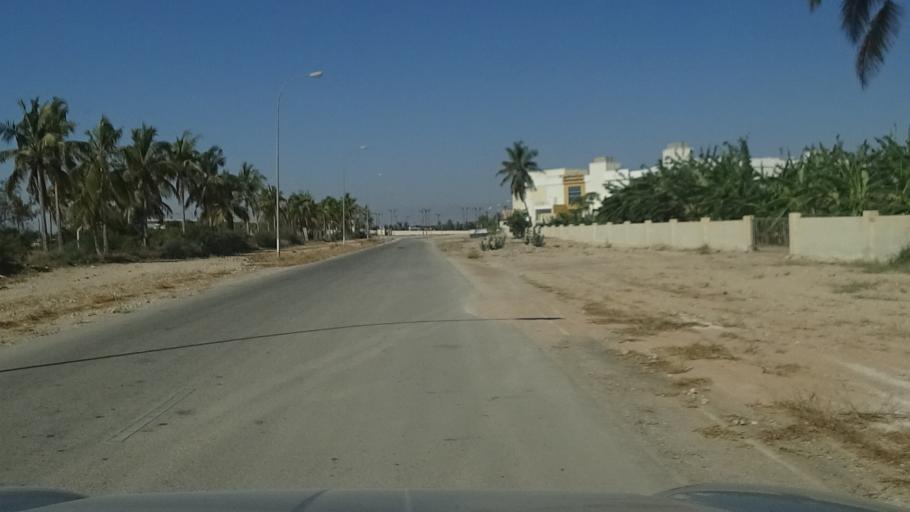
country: OM
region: Zufar
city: Salalah
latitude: 17.0345
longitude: 54.1503
